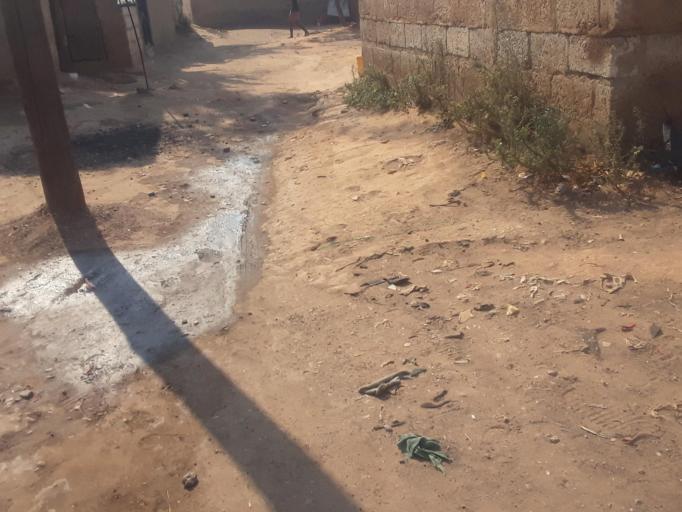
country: ZM
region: Lusaka
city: Lusaka
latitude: -15.3620
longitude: 28.2999
